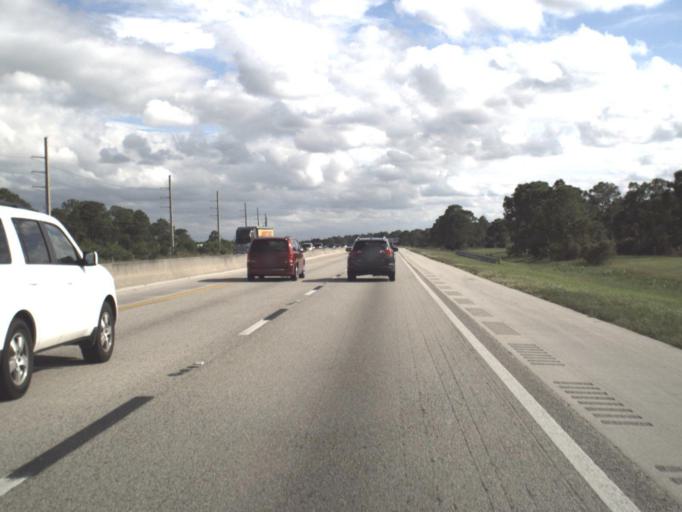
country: US
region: Florida
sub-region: Martin County
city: North River Shores
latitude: 27.1953
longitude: -80.3269
